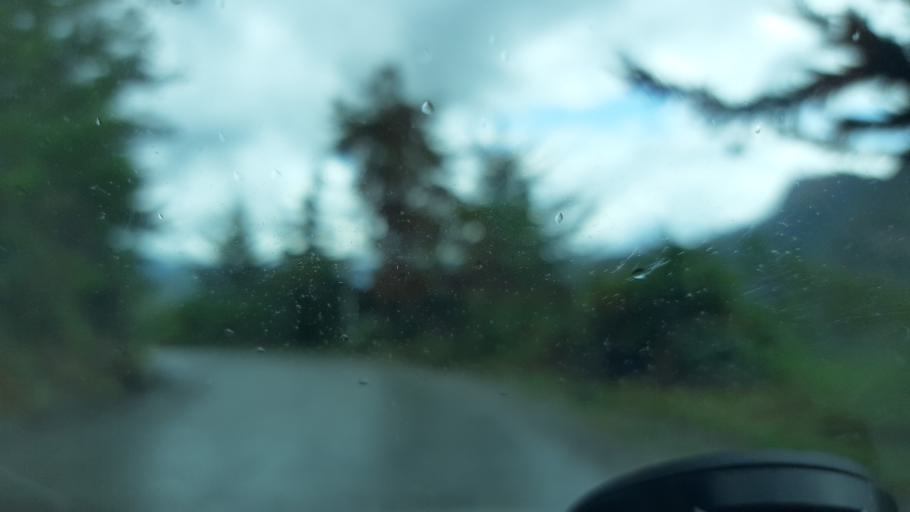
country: CO
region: Boyaca
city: Chinavita
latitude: 5.1554
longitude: -73.3696
